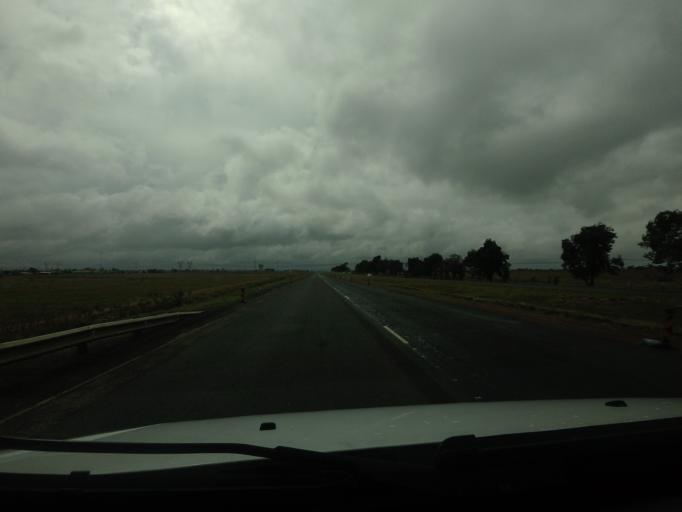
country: ZA
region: Mpumalanga
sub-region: Nkangala District Municipality
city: Witbank
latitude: -25.8717
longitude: 29.0992
